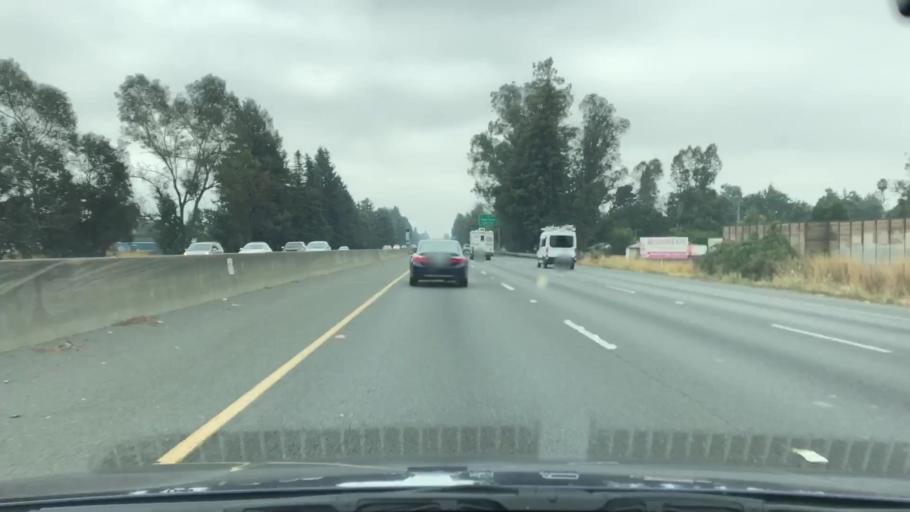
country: US
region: California
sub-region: Sonoma County
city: Roseland
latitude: 38.3958
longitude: -122.7162
